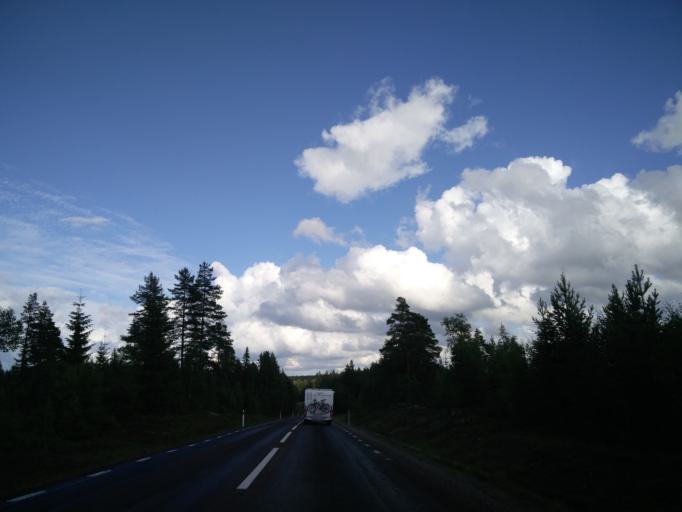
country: SE
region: Vaermland
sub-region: Hagfors Kommun
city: Ekshaerad
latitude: 60.4784
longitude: 13.3611
